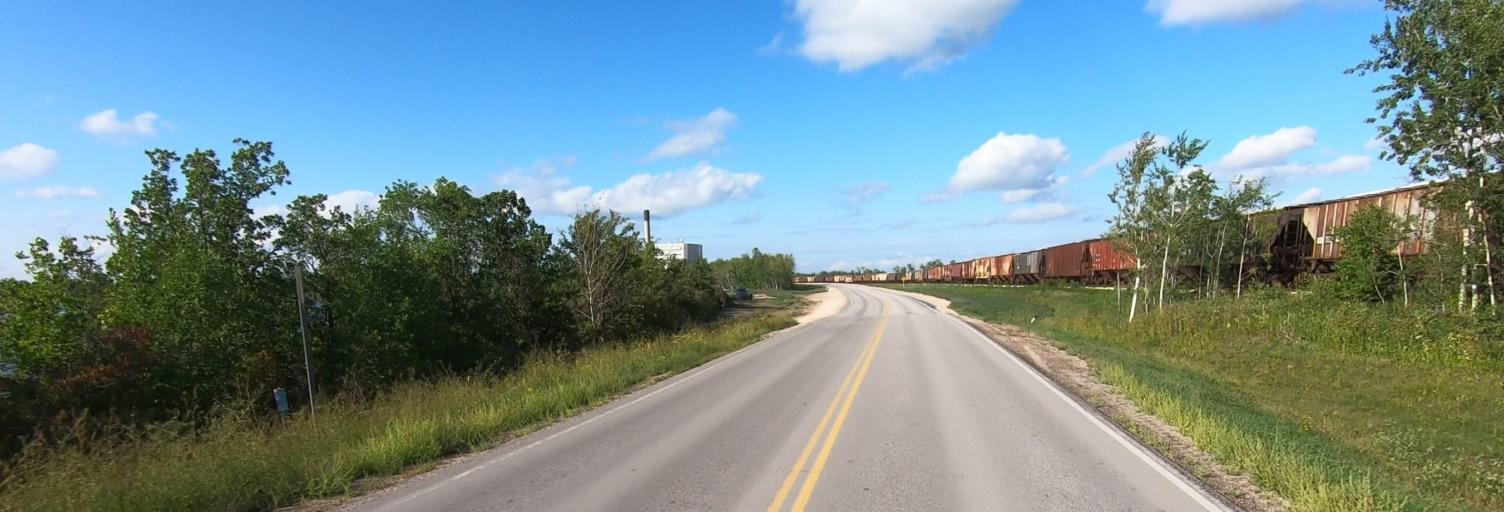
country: CA
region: Manitoba
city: Selkirk
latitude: 50.1267
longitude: -96.8543
